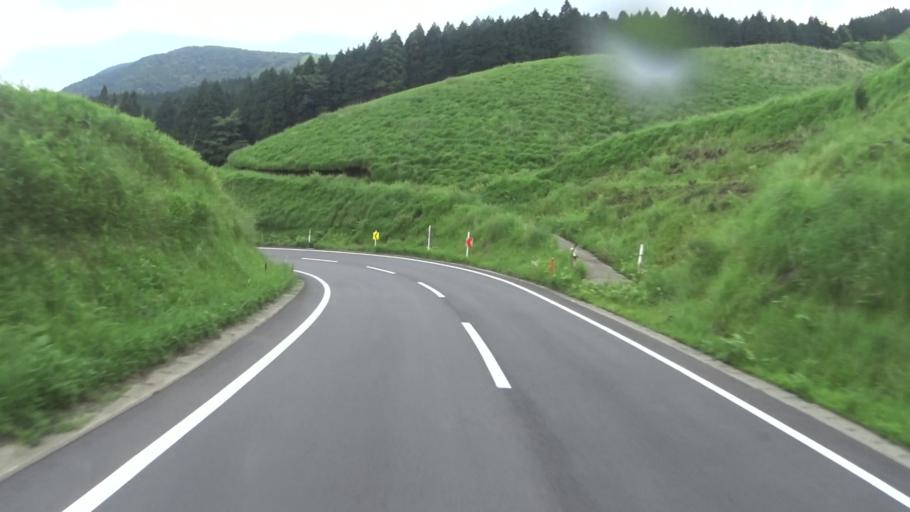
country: JP
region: Kumamoto
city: Aso
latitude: 32.9156
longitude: 130.9720
